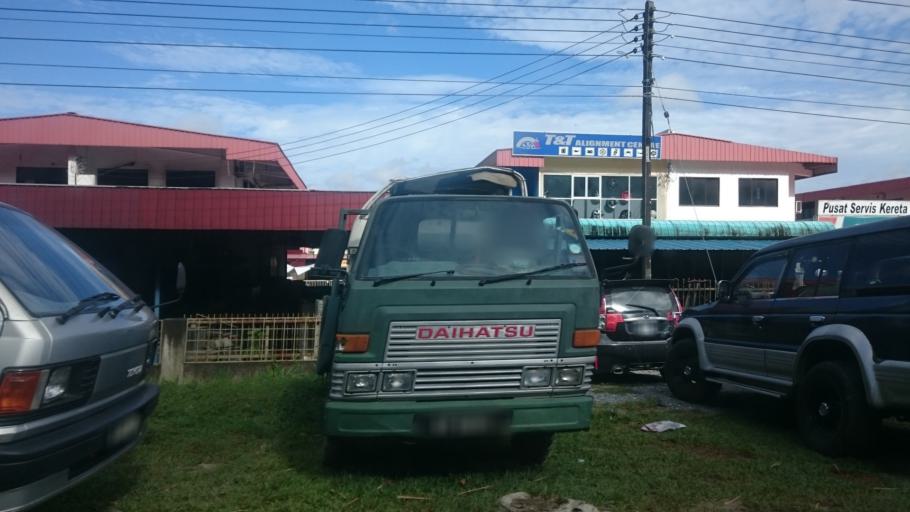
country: MY
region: Sarawak
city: Limbang
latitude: 4.7425
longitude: 115.0039
